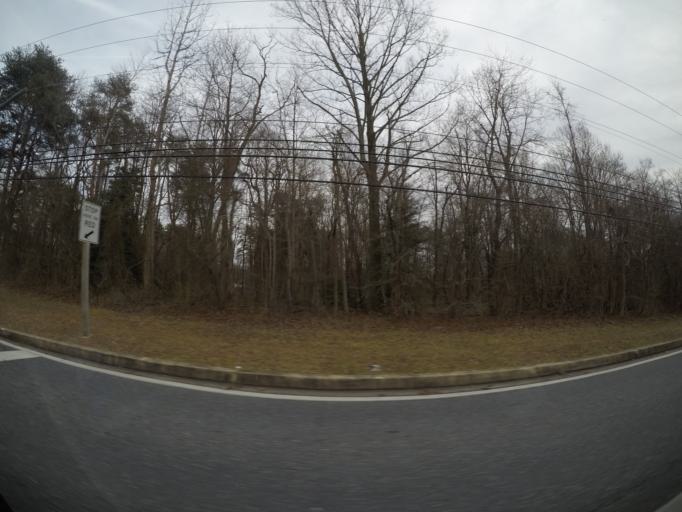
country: US
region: Maryland
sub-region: Anne Arundel County
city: Severn
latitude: 39.1466
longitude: -76.7262
